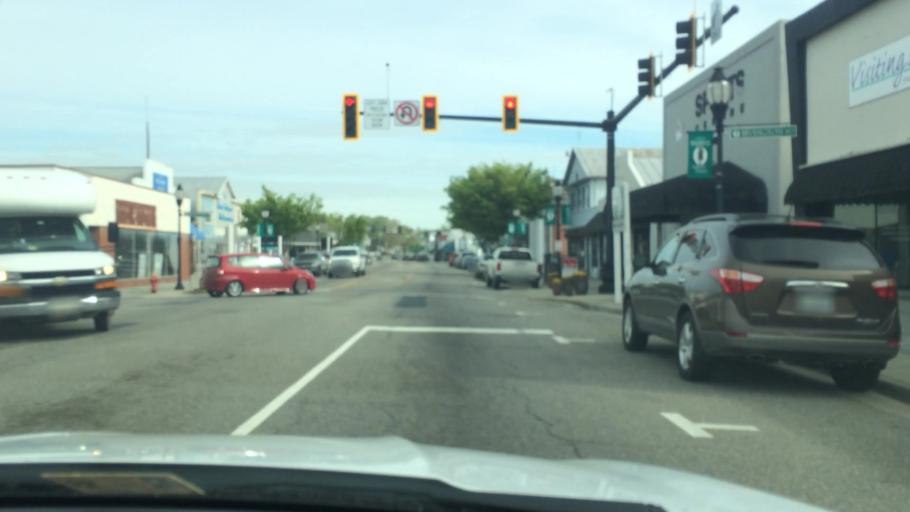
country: US
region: Virginia
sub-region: Lancaster County
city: Kilmarnock
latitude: 37.7095
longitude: -76.3798
